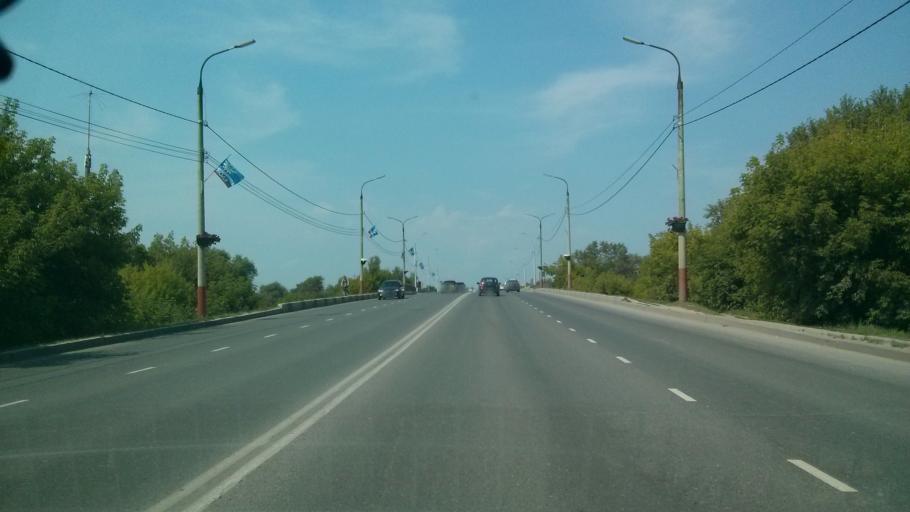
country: RU
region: Vladimir
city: Murom
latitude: 55.5634
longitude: 42.0436
